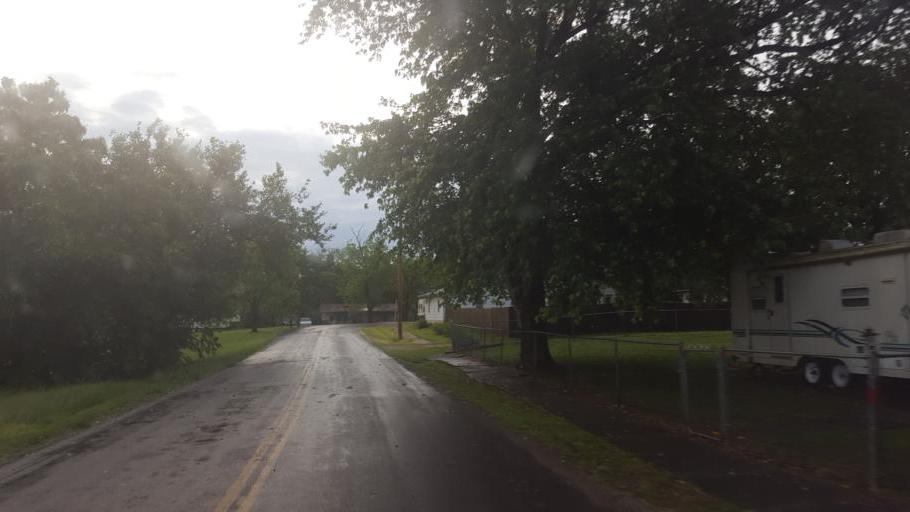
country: US
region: Missouri
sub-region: Moniteau County
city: California
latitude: 38.6398
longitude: -92.5673
